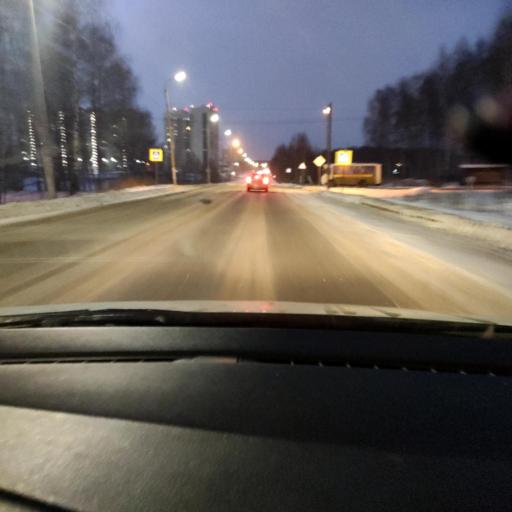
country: RU
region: Tatarstan
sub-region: Zelenodol'skiy Rayon
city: Zelenodolsk
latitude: 55.8692
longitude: 48.5698
